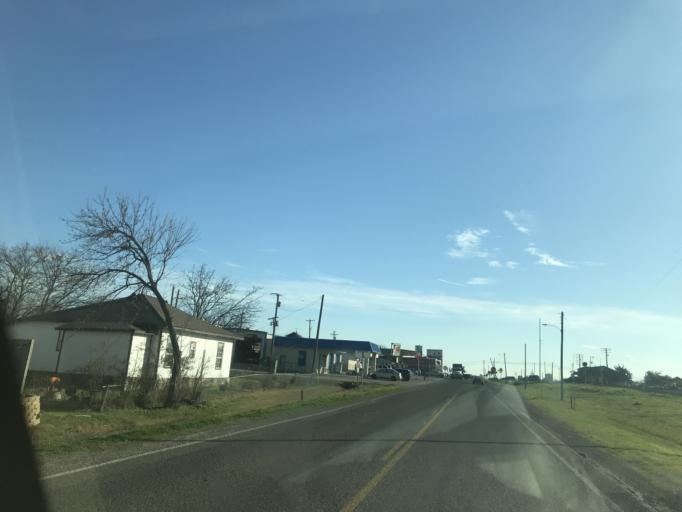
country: US
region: Texas
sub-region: Ellis County
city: Ferris
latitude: 32.5363
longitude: -96.6650
